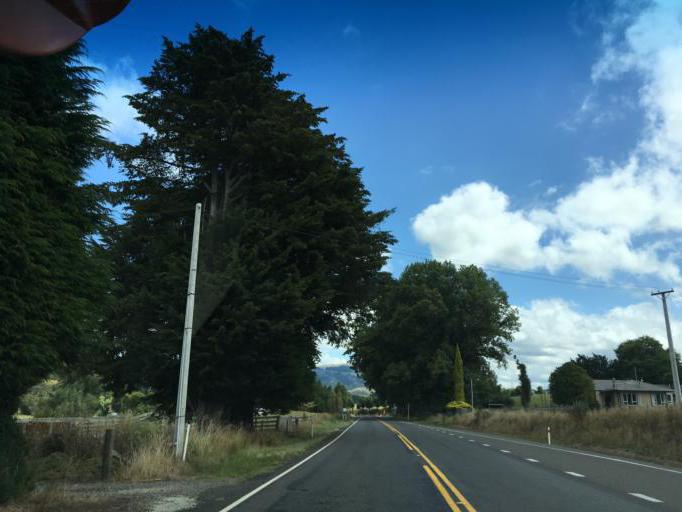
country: NZ
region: Hawke's Bay
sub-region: Napier City
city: Napier
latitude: -39.2025
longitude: 176.8842
